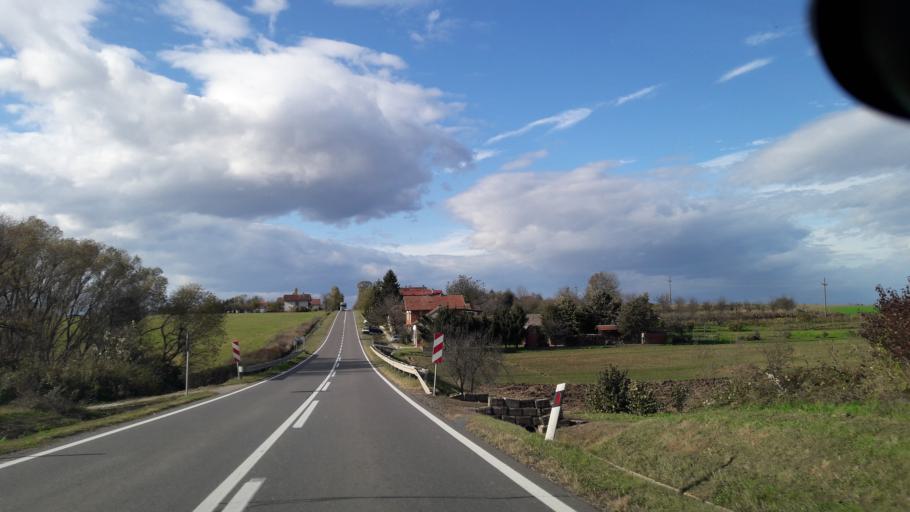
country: HR
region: Osjecko-Baranjska
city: Vukojevci
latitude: 45.4822
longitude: 18.1628
